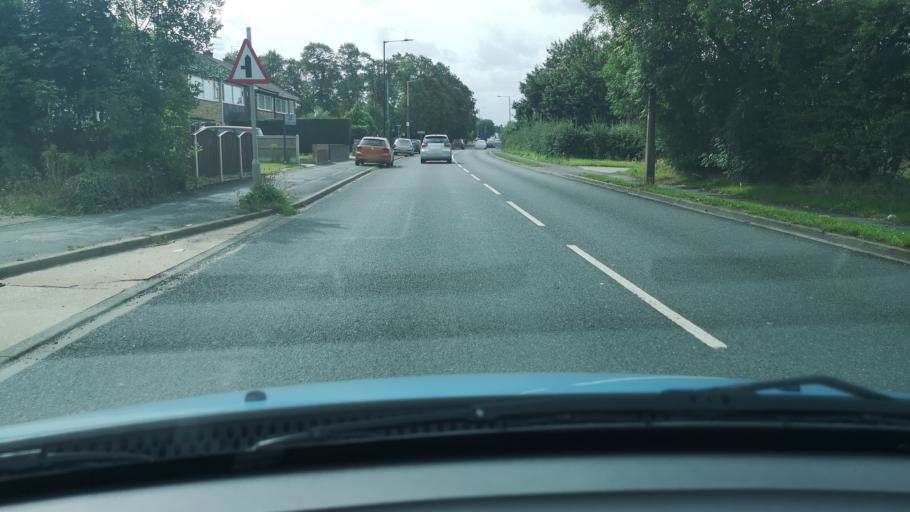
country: GB
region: England
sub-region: Doncaster
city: Kirk Sandall
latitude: 53.5587
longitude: -1.0745
